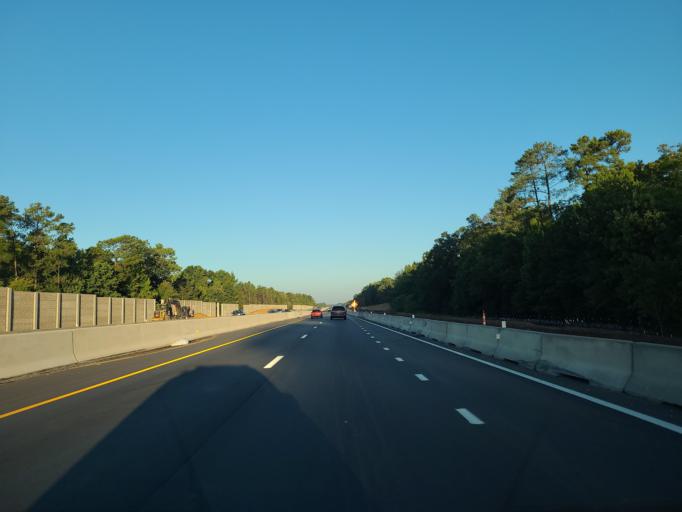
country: US
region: North Carolina
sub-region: Union County
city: Weddington
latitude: 35.0607
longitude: -80.7774
